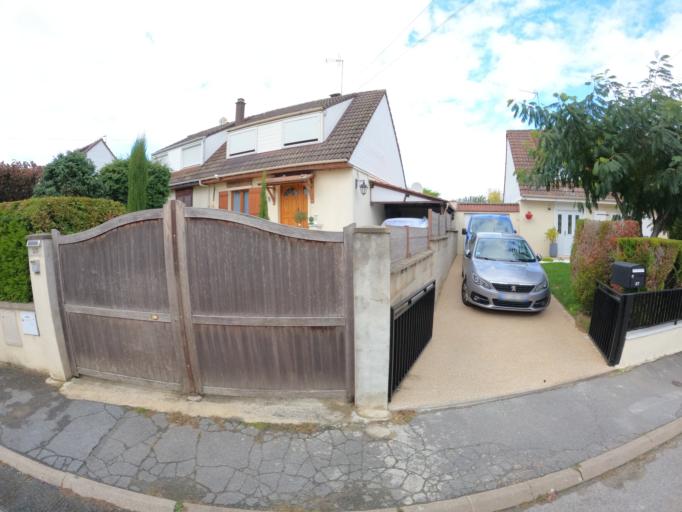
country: FR
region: Ile-de-France
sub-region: Departement de Seine-et-Marne
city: Saint-Germain-sur-Morin
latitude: 48.8862
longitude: 2.8420
